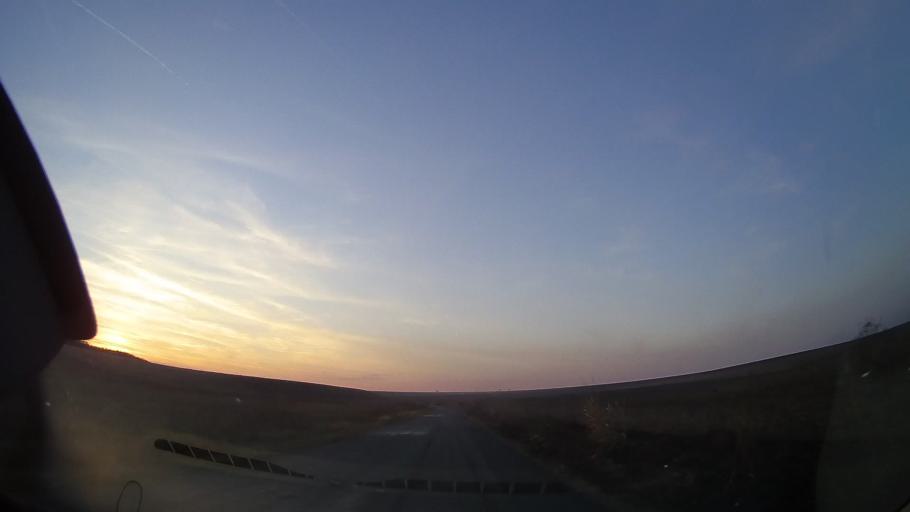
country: RO
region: Constanta
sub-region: Comuna Mereni
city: Mereni
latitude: 44.0182
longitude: 28.2993
